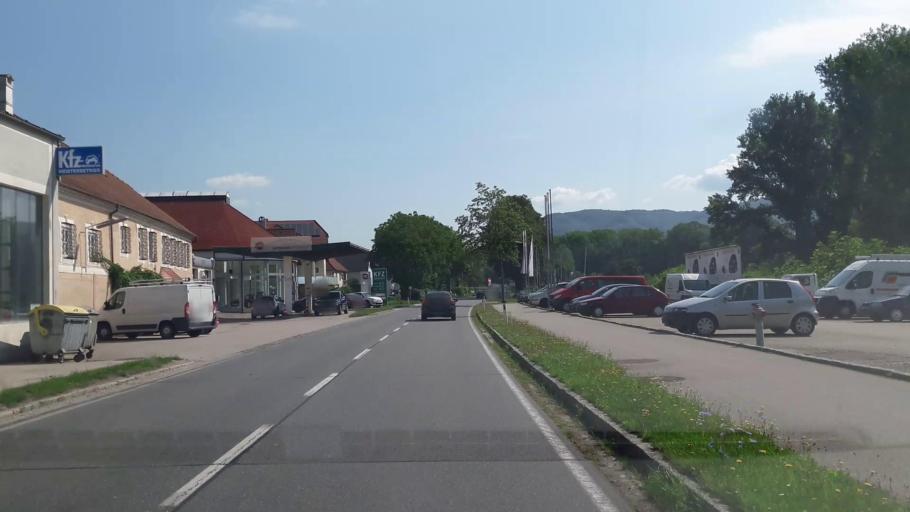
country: AT
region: Lower Austria
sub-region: Politischer Bezirk Melk
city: Emmersdorf an der Donau
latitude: 48.2517
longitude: 15.3521
